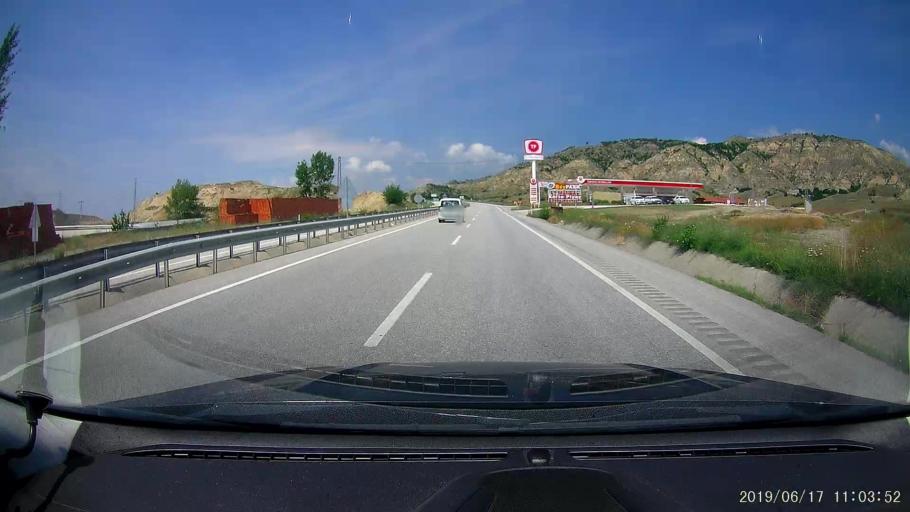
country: TR
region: Kastamonu
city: Tosya
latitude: 41.0198
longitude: 34.1073
